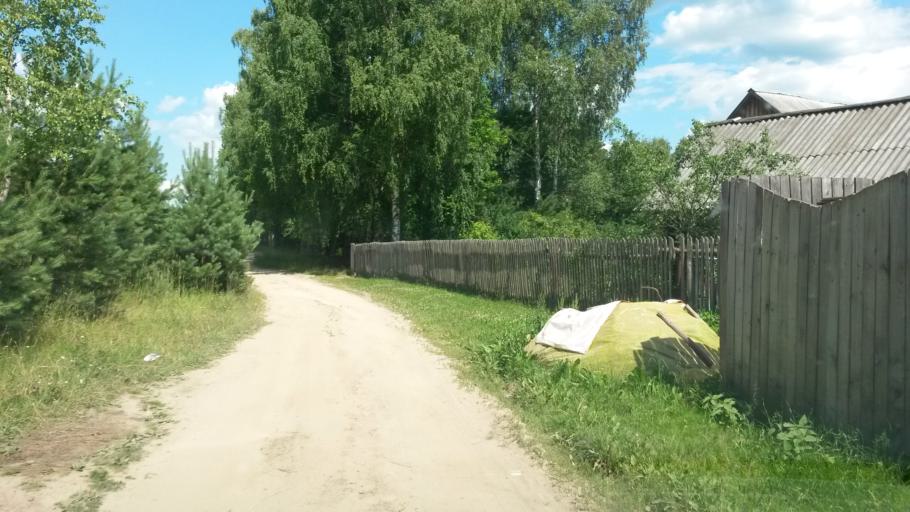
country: RU
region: Ivanovo
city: Zarechnyy
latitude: 57.4977
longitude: 42.3293
